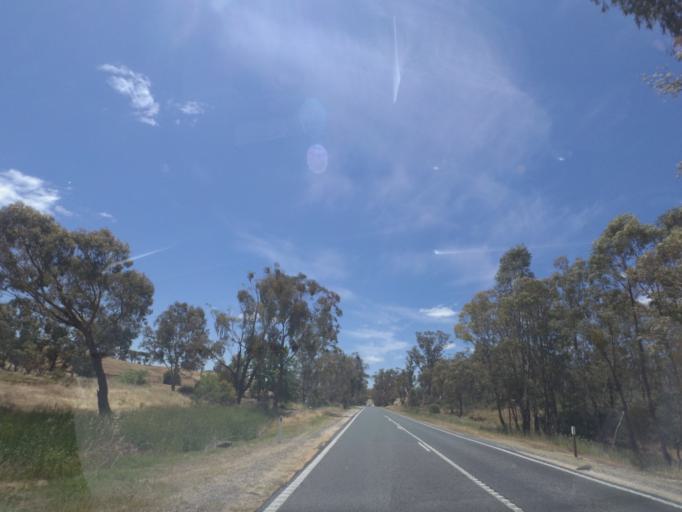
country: AU
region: Victoria
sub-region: Mount Alexander
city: Castlemaine
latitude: -37.1985
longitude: 144.1463
